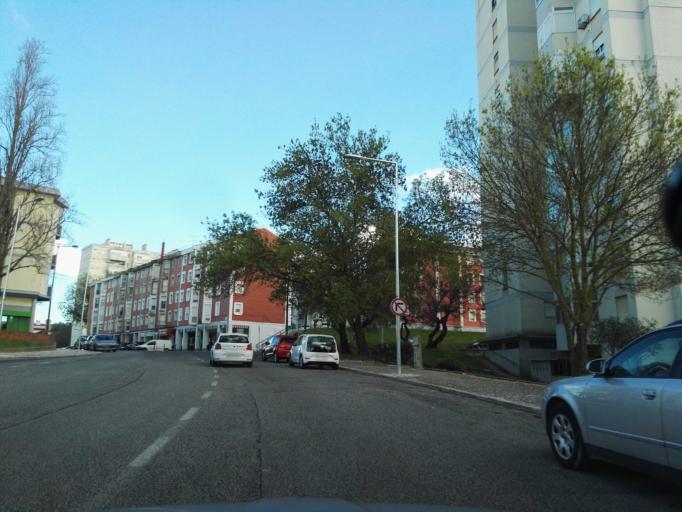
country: PT
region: Lisbon
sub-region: Loures
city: Moscavide
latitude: 38.7661
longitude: -9.1175
